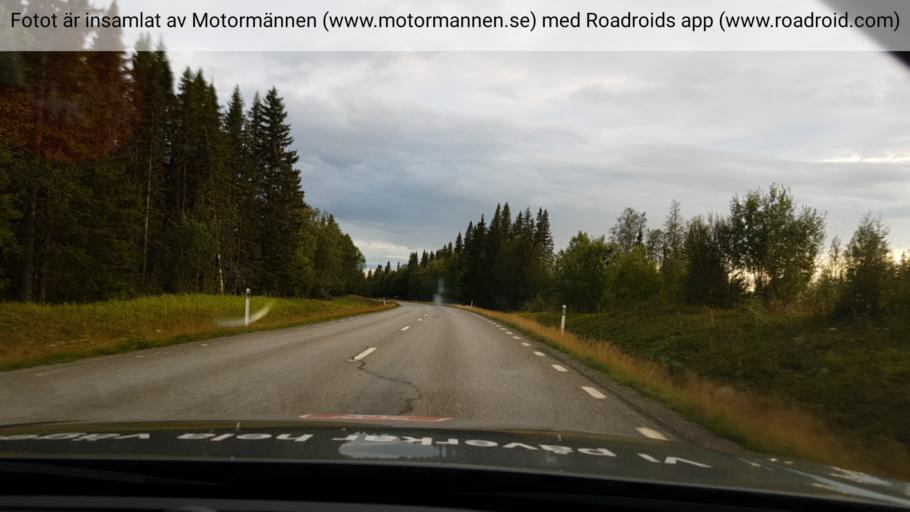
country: SE
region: Jaemtland
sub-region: OEstersunds Kommun
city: Lit
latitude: 63.4402
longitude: 15.1321
